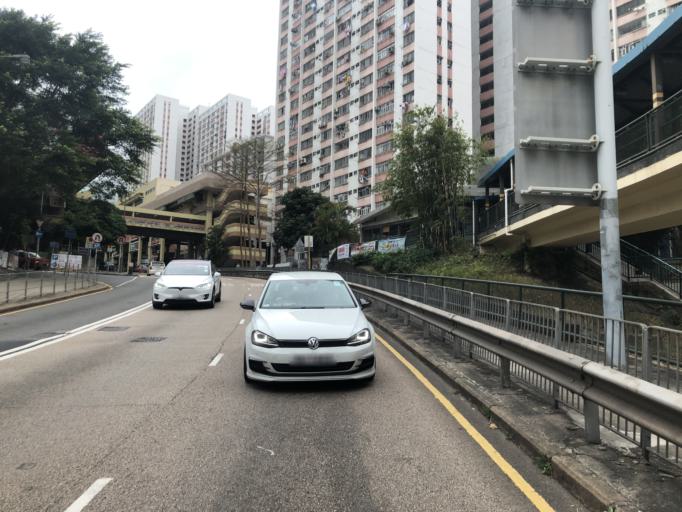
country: HK
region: Wong Tai Sin
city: Wong Tai Sin
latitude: 22.3336
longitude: 114.2137
